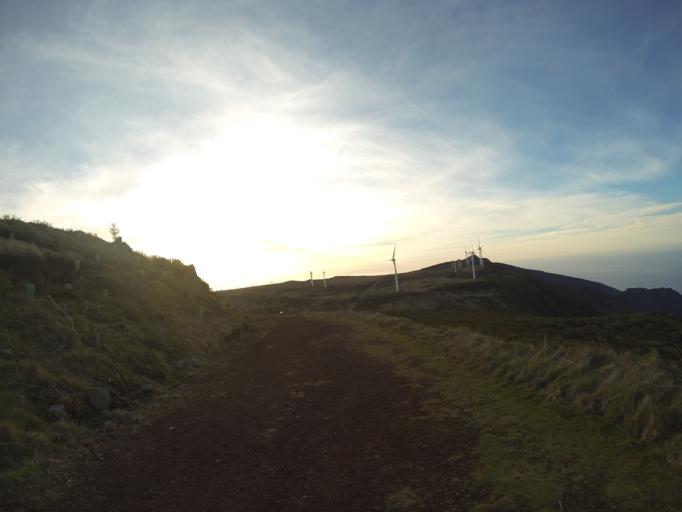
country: PT
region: Madeira
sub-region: Sao Vicente
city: Sao Vicente
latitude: 32.7564
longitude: -17.0554
